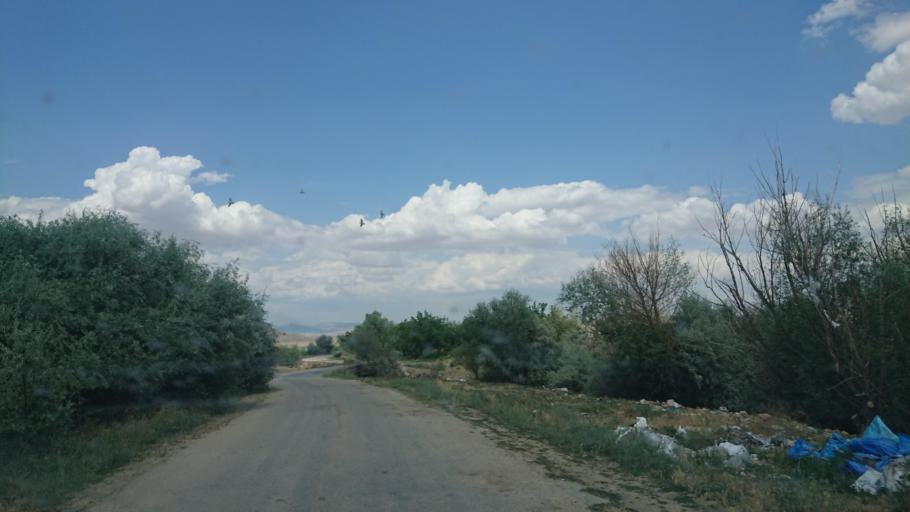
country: TR
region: Aksaray
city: Sariyahsi
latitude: 38.9669
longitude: 33.8908
